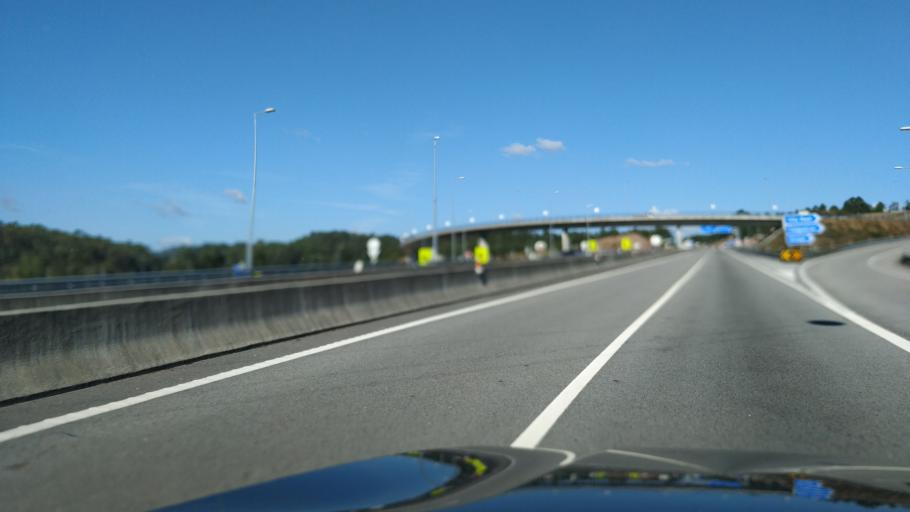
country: PT
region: Porto
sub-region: Vila Nova de Gaia
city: Sandim
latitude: 41.0359
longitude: -8.4926
